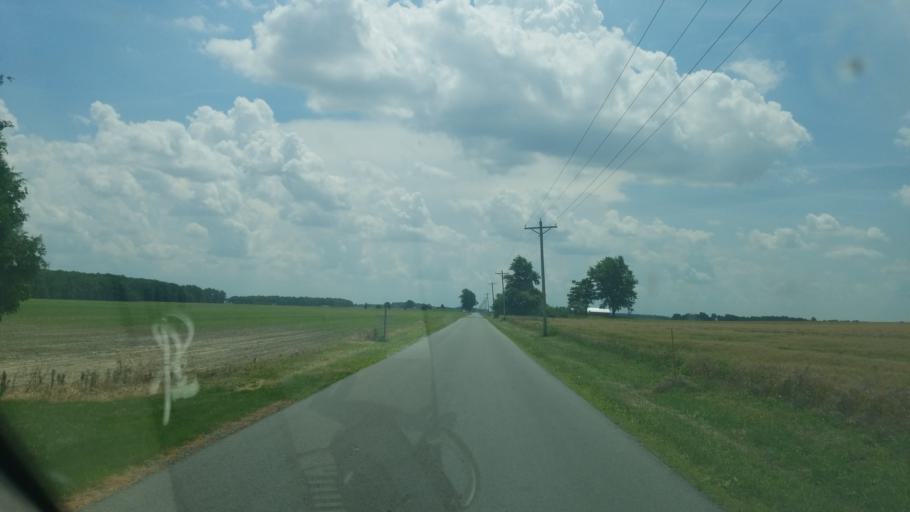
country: US
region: Ohio
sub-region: Hancock County
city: Arlington
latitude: 40.8462
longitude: -83.5999
